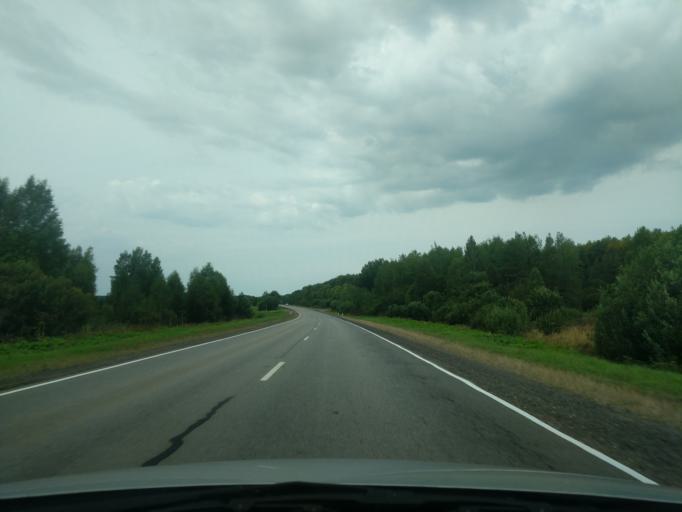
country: RU
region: Kirov
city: Svecha
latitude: 58.2739
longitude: 47.7541
